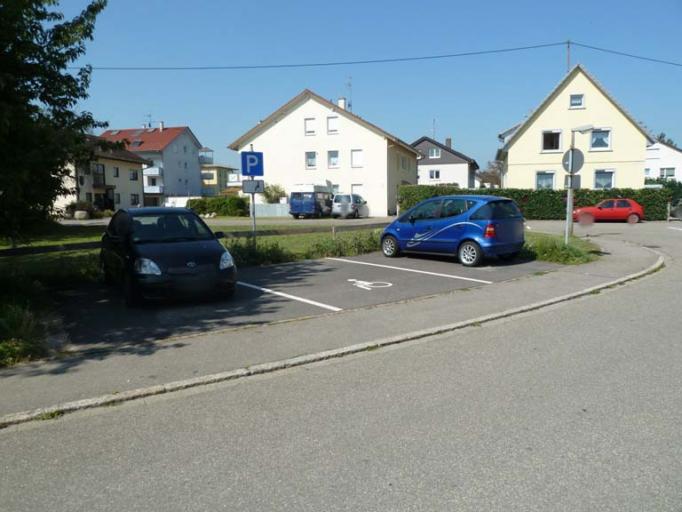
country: DE
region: Baden-Wuerttemberg
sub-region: Freiburg Region
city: Eimeldingen
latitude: 47.6279
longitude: 7.5954
